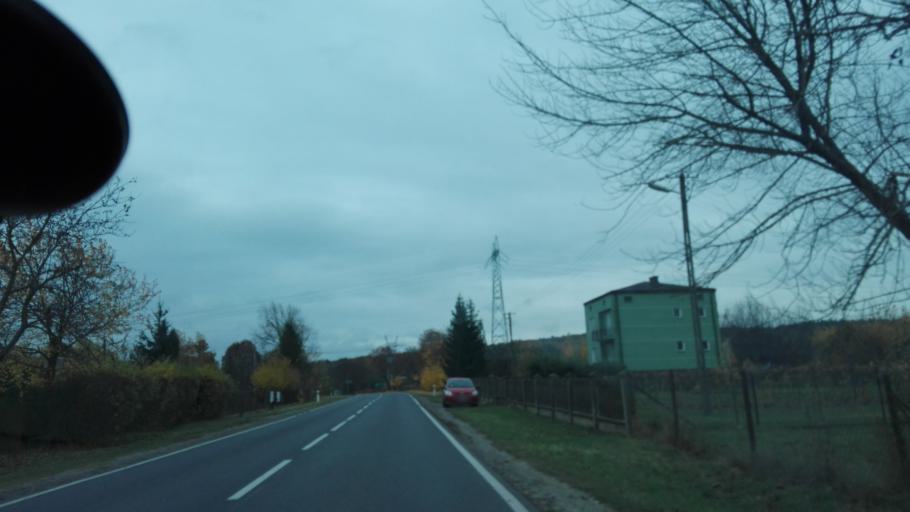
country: PL
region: Lublin Voivodeship
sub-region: Powiat pulawski
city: Pulawy
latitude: 51.4311
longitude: 21.9141
